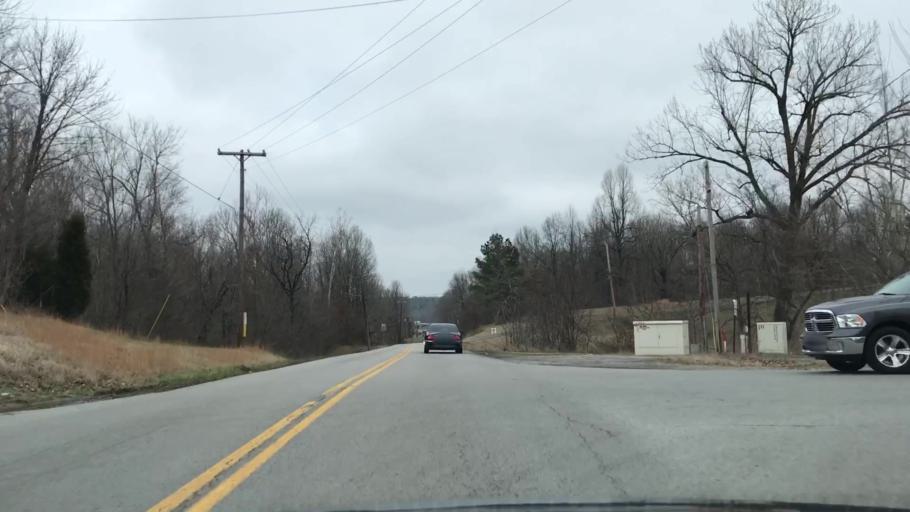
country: US
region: Kentucky
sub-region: Muhlenberg County
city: Morehead
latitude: 37.2422
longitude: -87.1942
